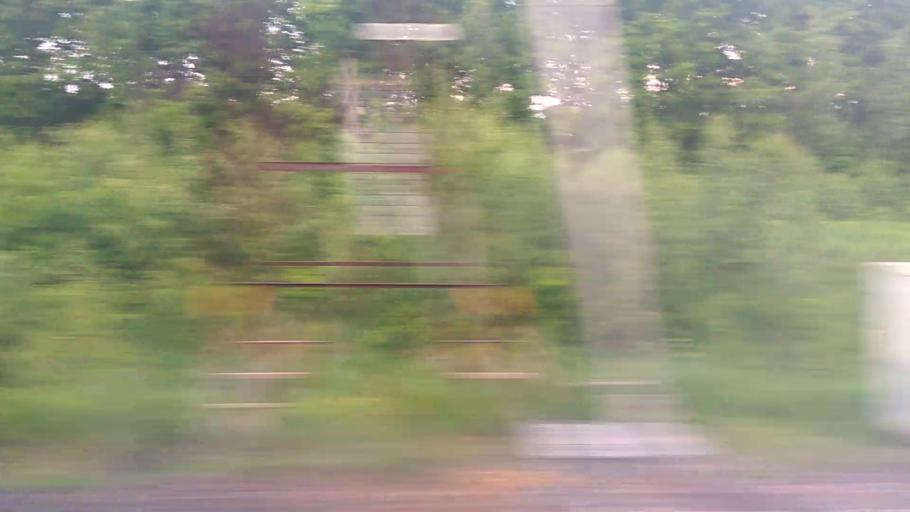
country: RU
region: Moskovskaya
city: Mikhnevo
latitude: 55.0711
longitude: 37.9822
